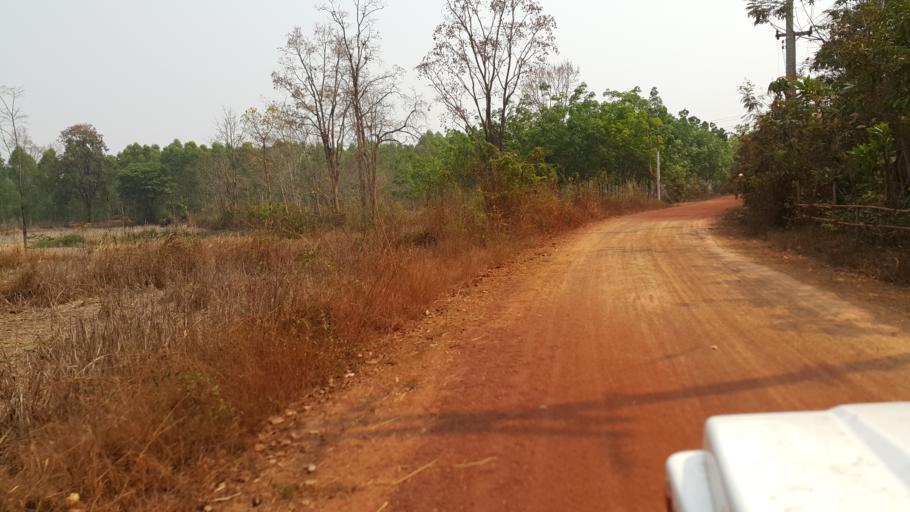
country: TH
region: Nakhon Phanom
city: Ban Phaeng
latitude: 17.8301
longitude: 104.2474
